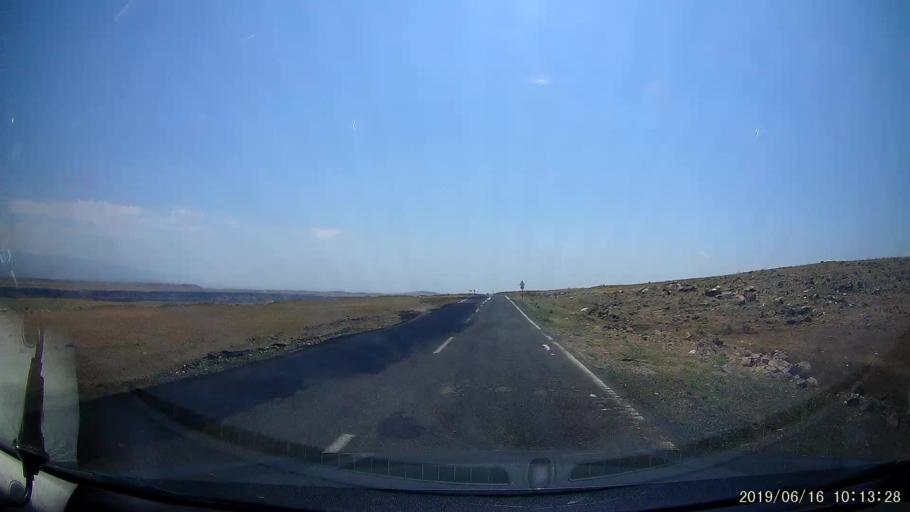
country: TR
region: Igdir
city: Tuzluca
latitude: 40.1925
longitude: 43.6430
